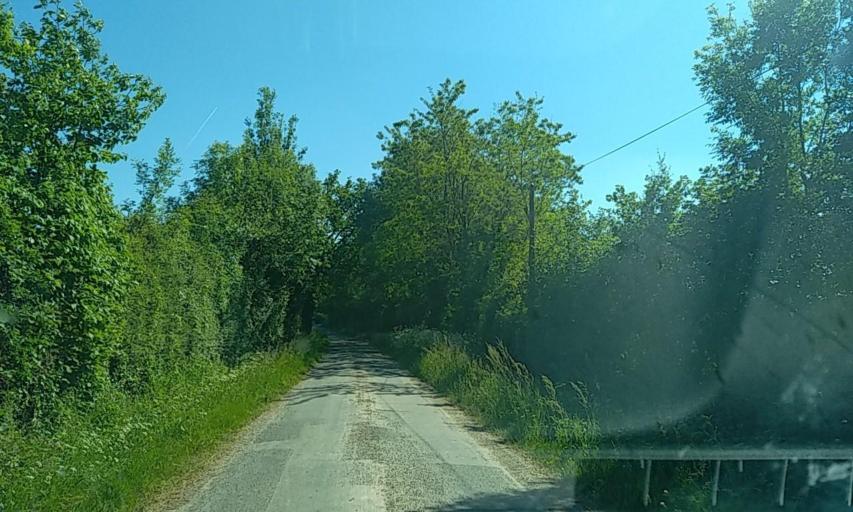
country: FR
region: Poitou-Charentes
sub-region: Departement des Deux-Sevres
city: Boisme
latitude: 46.7965
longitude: -0.4642
